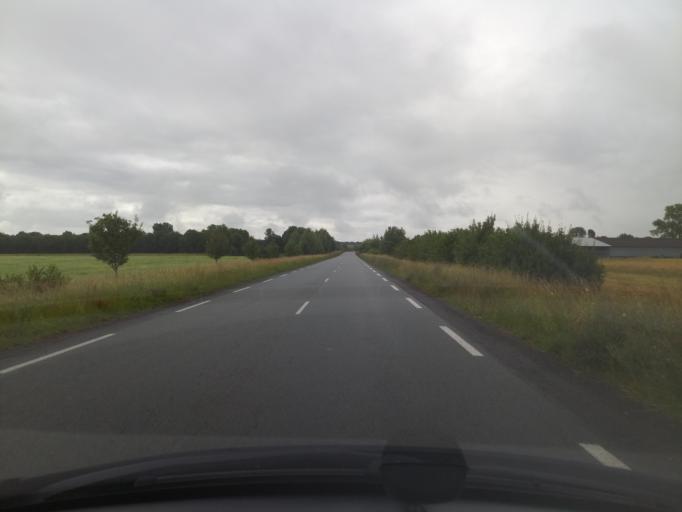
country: FR
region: Poitou-Charentes
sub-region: Departement de la Charente-Maritime
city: Courcon
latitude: 46.1923
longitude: -0.8605
